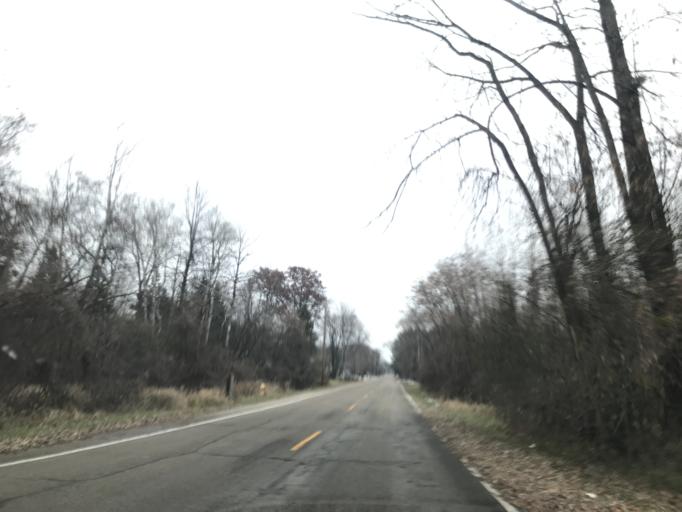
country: US
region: Wisconsin
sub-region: Marinette County
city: Marinette
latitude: 45.0780
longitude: -87.6283
